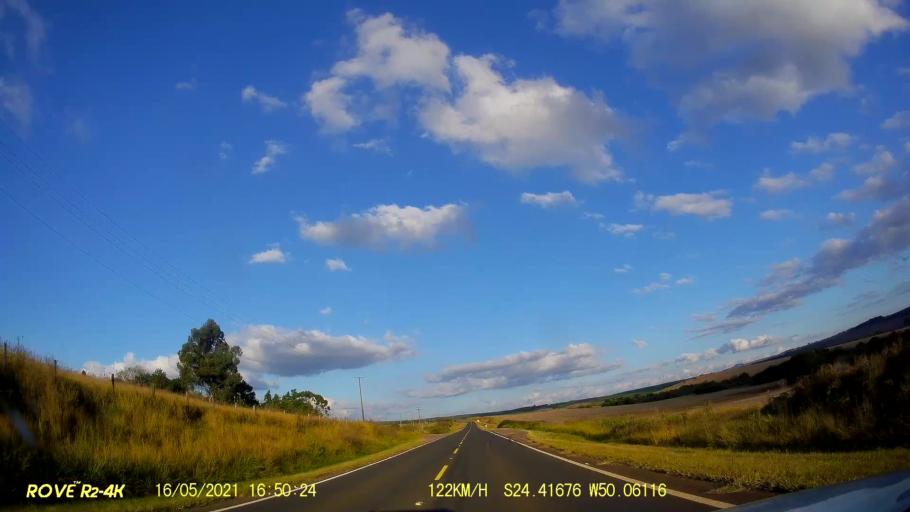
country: BR
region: Parana
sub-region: Pirai Do Sul
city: Pirai do Sul
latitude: -24.4172
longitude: -50.0605
